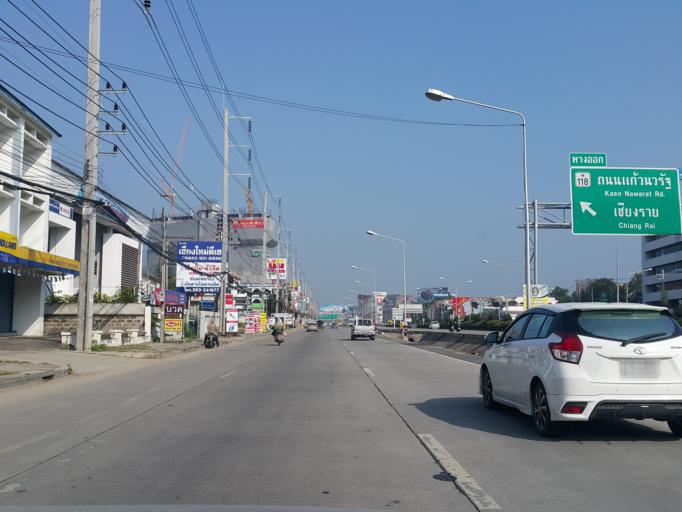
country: TH
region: Chiang Mai
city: Chiang Mai
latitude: 18.7973
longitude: 99.0208
